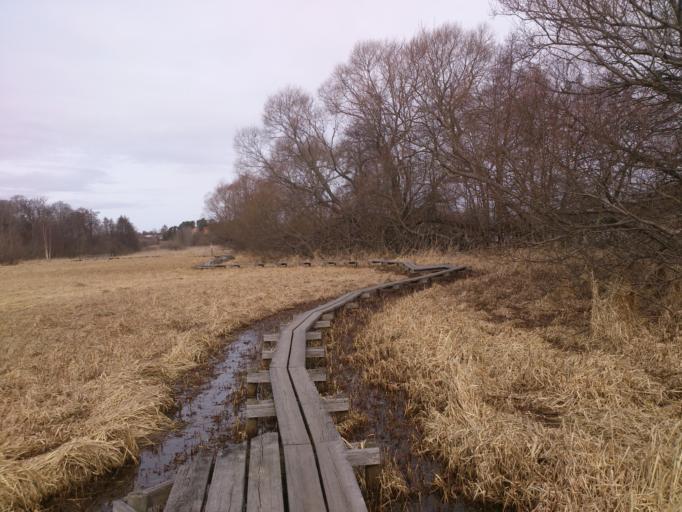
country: SE
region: Uppsala
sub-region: Uppsala Kommun
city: Saevja
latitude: 59.8033
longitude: 17.6673
